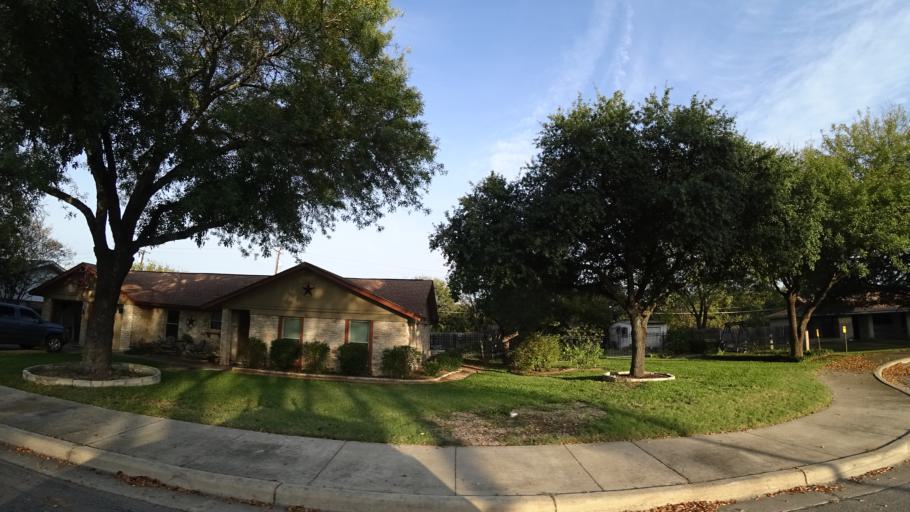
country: US
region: Texas
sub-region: Williamson County
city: Round Rock
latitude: 30.5041
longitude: -97.6701
